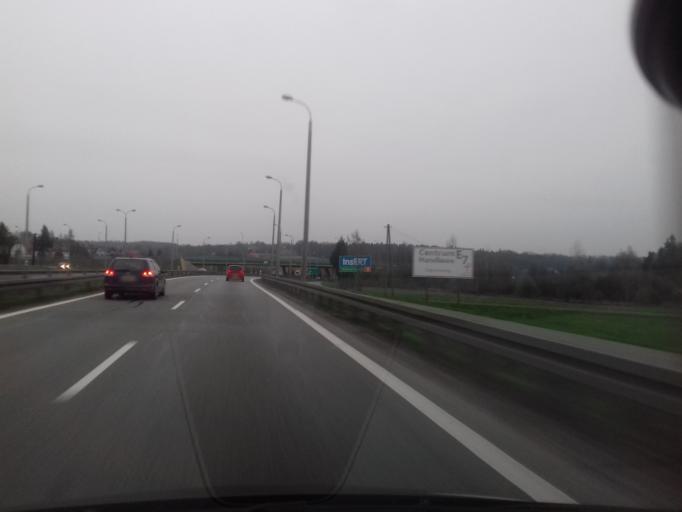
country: PL
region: Lesser Poland Voivodeship
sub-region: Powiat myslenicki
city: Glogoczow
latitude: 49.9059
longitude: 19.8701
